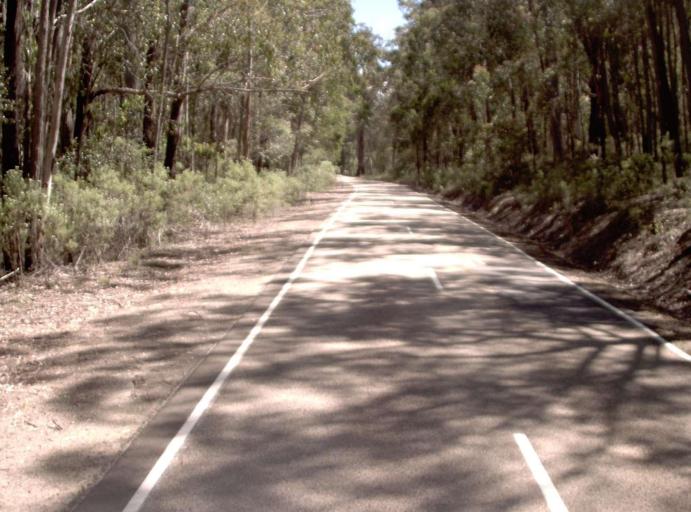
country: AU
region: Victoria
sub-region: East Gippsland
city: Lakes Entrance
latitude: -37.2888
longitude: 148.2558
